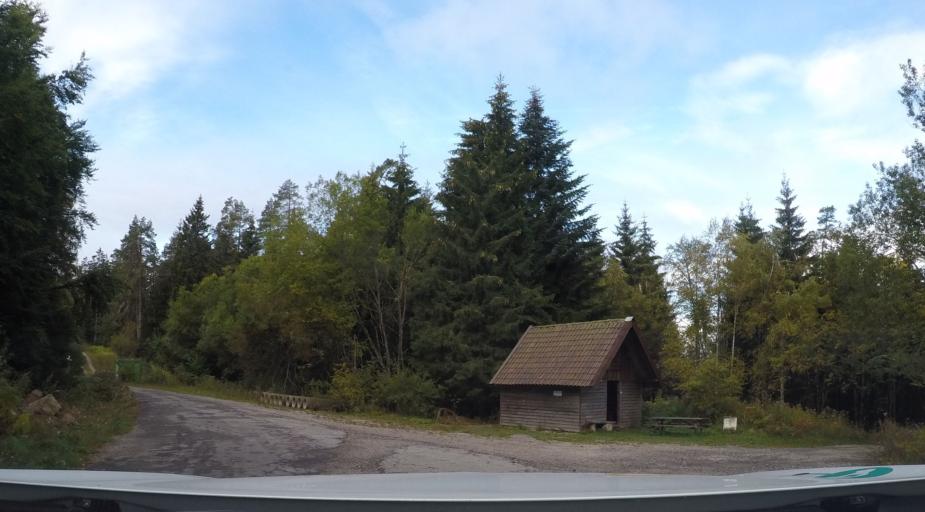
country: DE
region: Baden-Wuerttemberg
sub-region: Karlsruhe Region
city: Biberach
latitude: 48.5655
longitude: 8.3262
